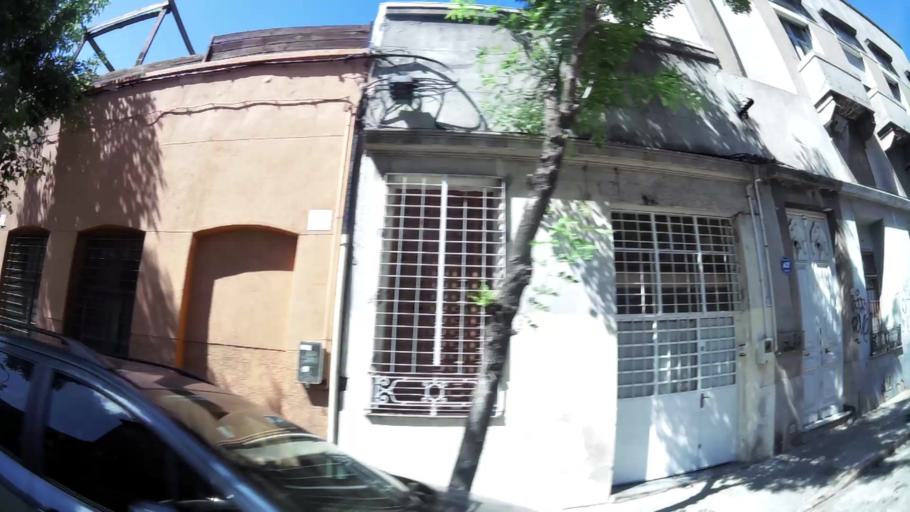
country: UY
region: Montevideo
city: Montevideo
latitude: -34.9055
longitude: -56.1781
